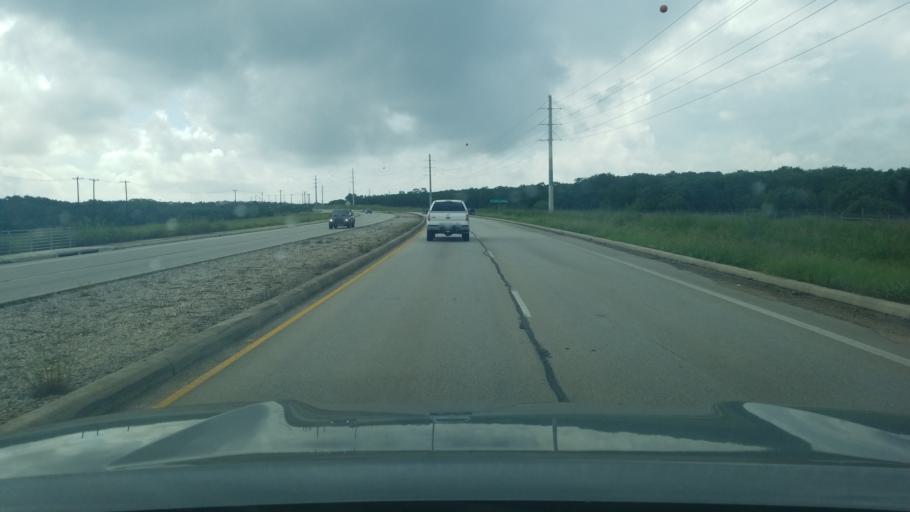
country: US
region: Texas
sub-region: Bexar County
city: Hollywood Park
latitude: 29.6562
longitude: -98.5213
